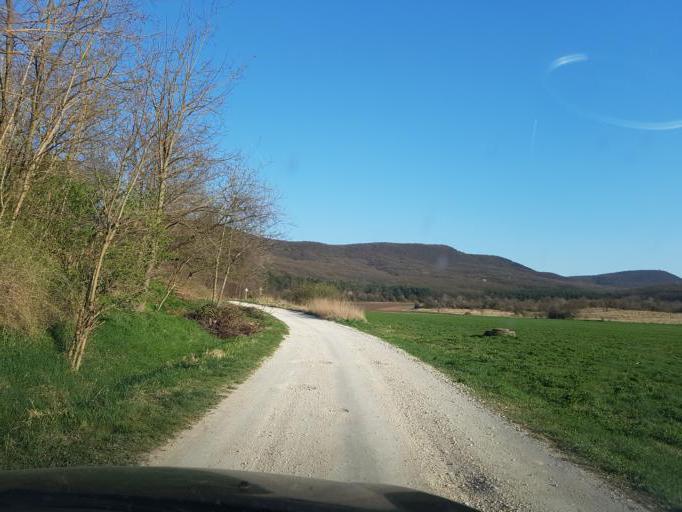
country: HU
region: Komarom-Esztergom
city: Piliscsev
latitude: 47.6745
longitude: 18.8238
